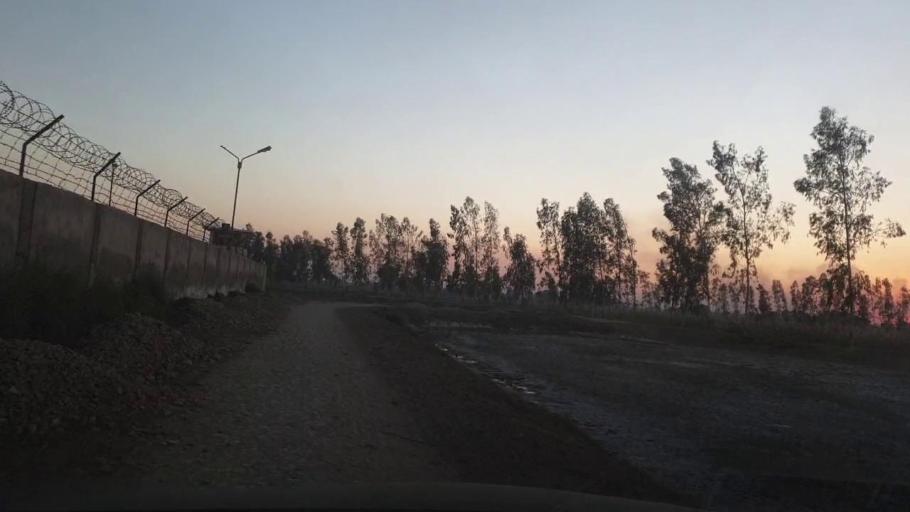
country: PK
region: Sindh
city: Ghotki
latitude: 28.0453
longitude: 69.3568
